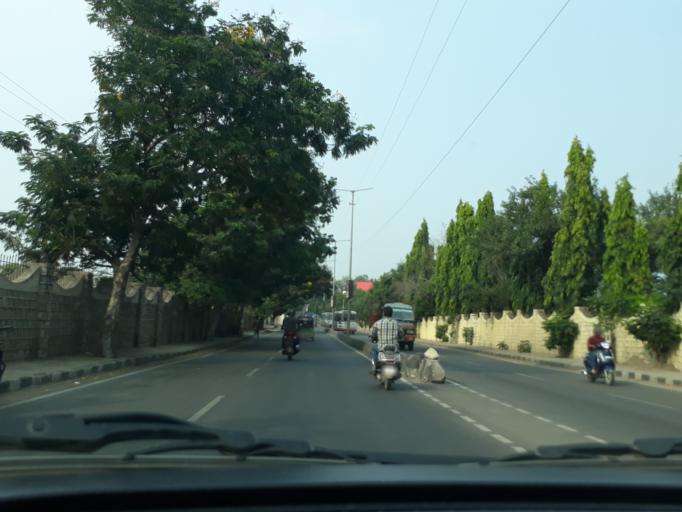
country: IN
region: Telangana
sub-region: Hyderabad
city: Malkajgiri
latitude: 17.4448
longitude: 78.4911
